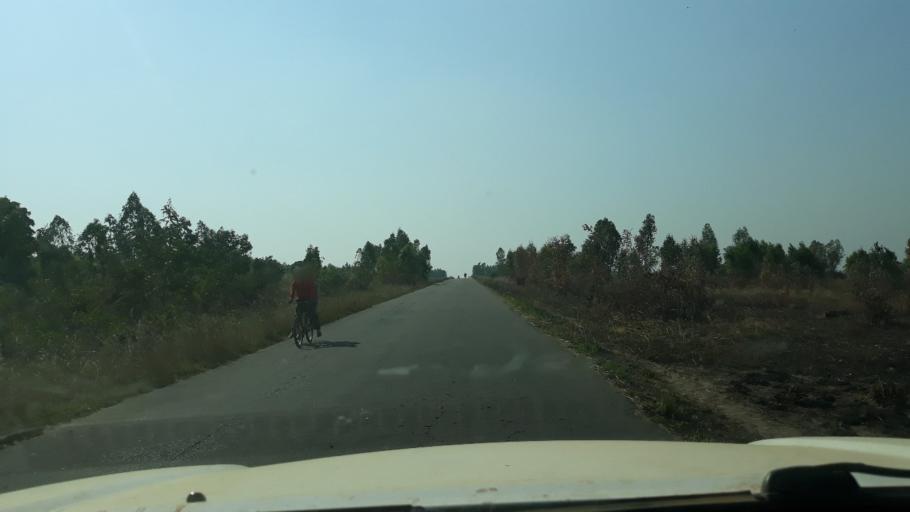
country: BI
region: Cibitoke
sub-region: Commune of Buganda
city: Buganda
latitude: -3.0452
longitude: 29.1146
